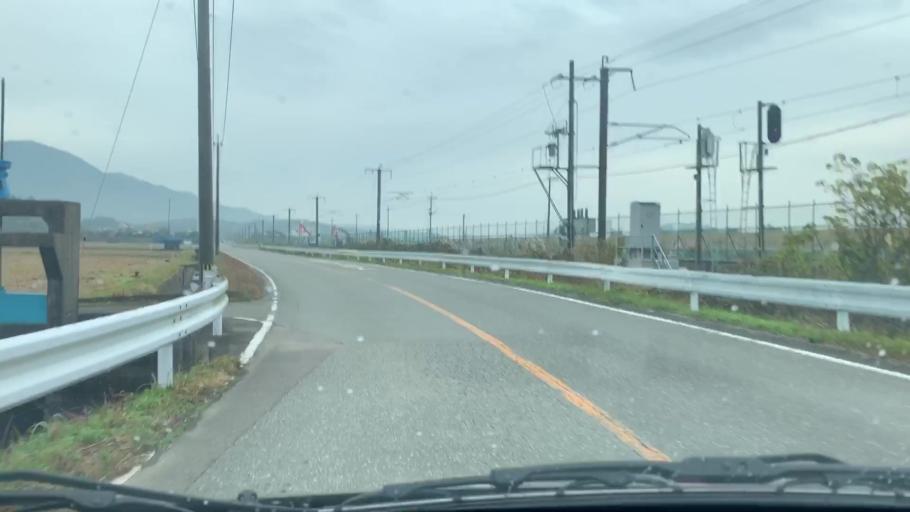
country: JP
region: Saga Prefecture
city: Takeocho-takeo
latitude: 33.2141
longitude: 130.0651
